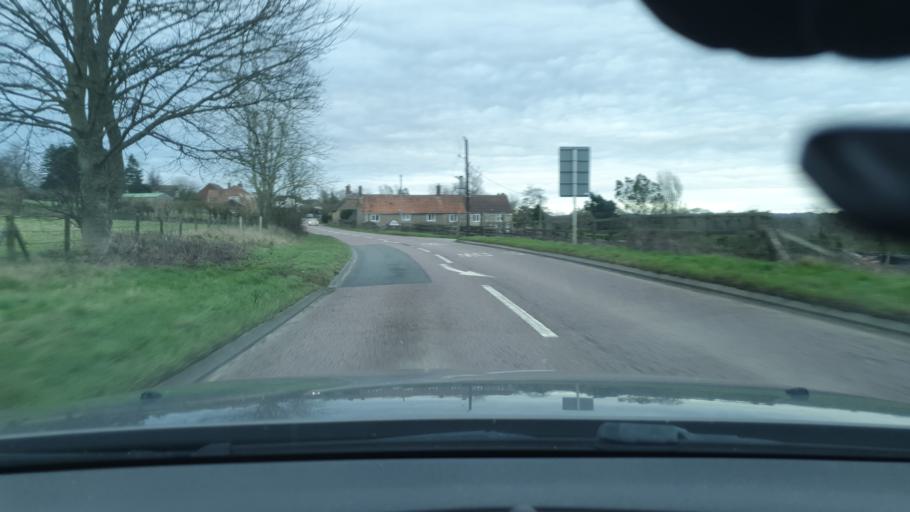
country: GB
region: England
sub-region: Wiltshire
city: Seend
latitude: 51.3409
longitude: -2.1047
